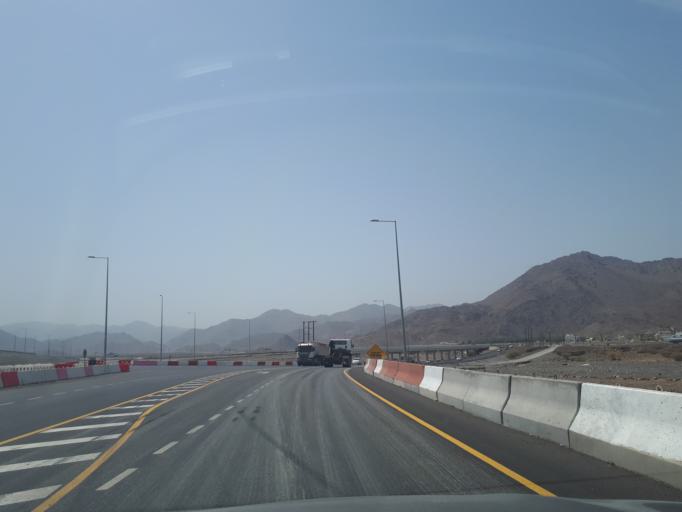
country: OM
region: Muhafazat ad Dakhiliyah
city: Sufalat Sama'il
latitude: 23.2637
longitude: 58.1037
